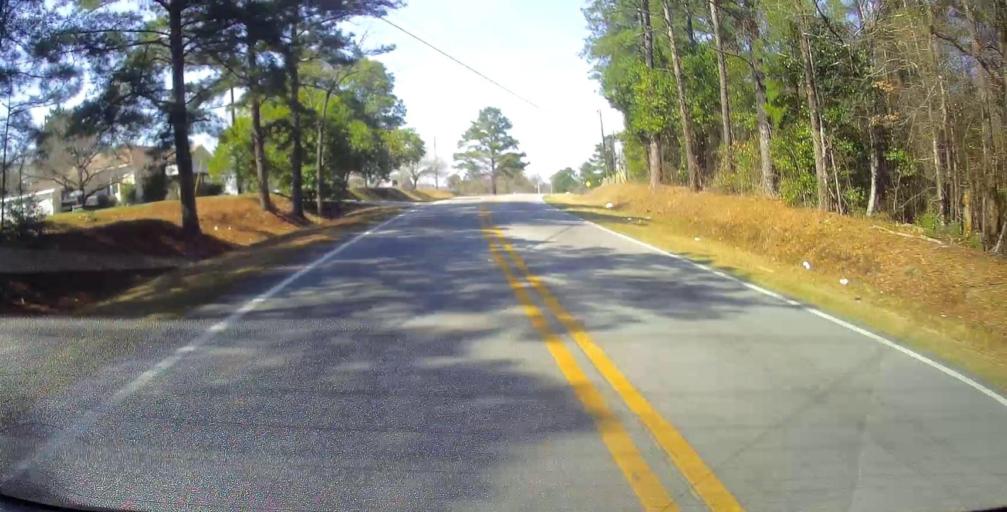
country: US
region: Georgia
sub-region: Bibb County
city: Macon
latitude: 32.8841
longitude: -83.5747
